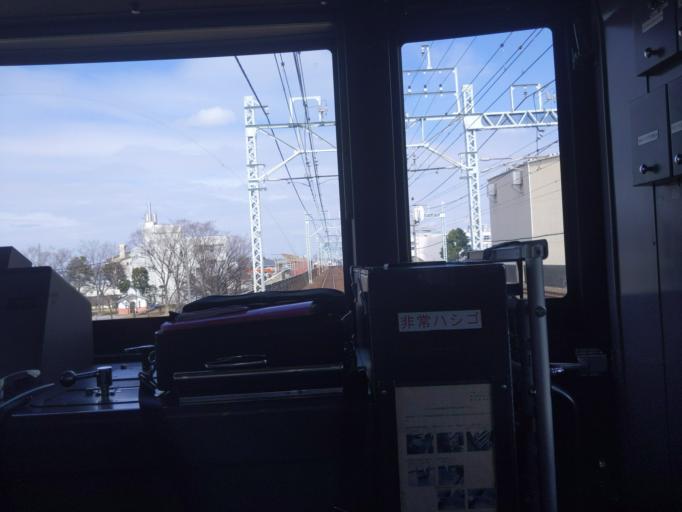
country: JP
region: Saitama
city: Soka
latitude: 35.8073
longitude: 139.7957
